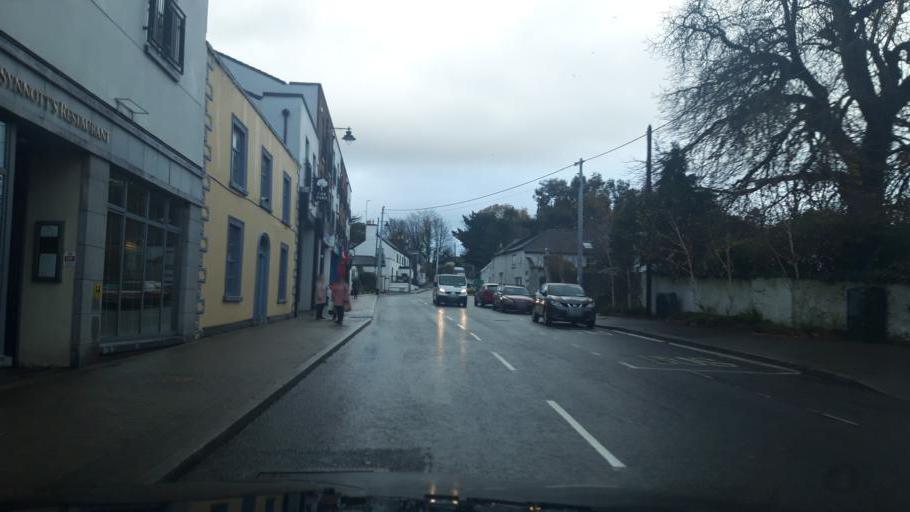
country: IE
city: Newtownmountkennedy
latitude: 53.0921
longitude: -6.1122
